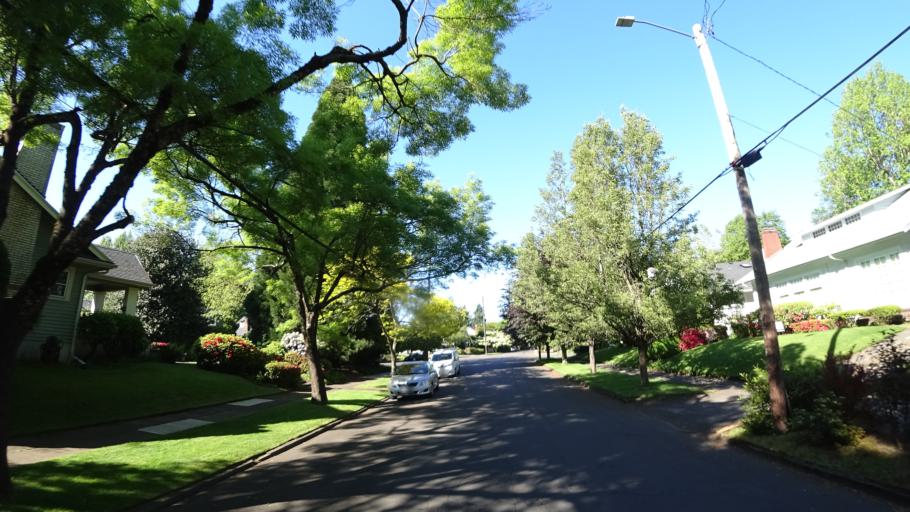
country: US
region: Oregon
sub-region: Multnomah County
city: Portland
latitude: 45.5286
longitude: -122.6283
